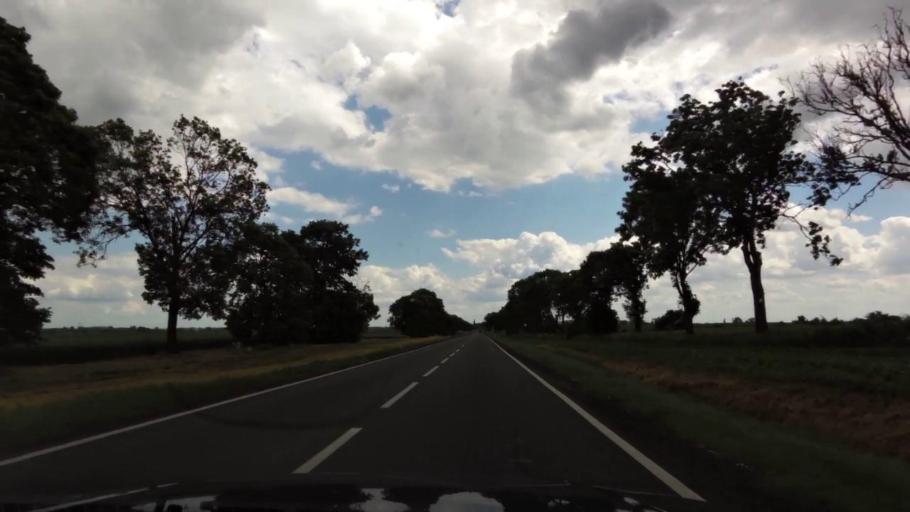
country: PL
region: West Pomeranian Voivodeship
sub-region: Powiat mysliborski
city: Mysliborz
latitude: 52.9601
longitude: 14.7611
